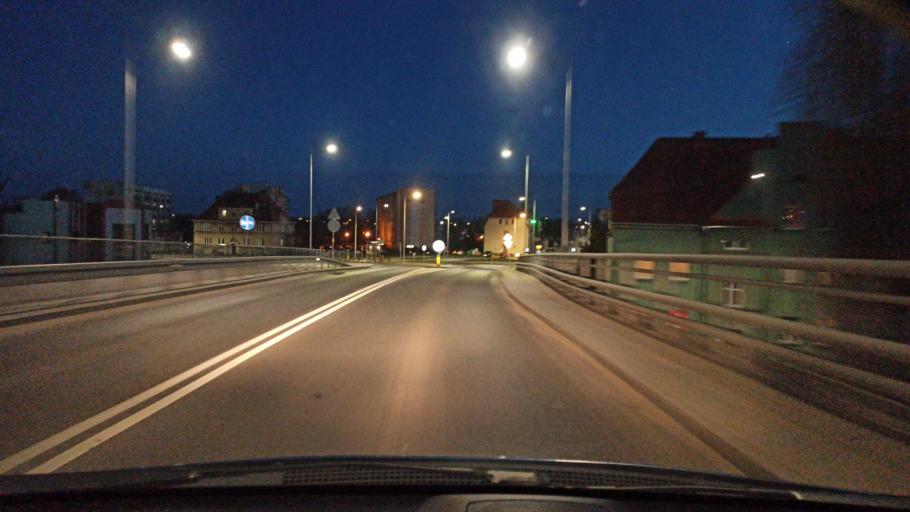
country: PL
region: Warmian-Masurian Voivodeship
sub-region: Powiat elblaski
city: Elblag
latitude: 54.1508
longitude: 19.4127
